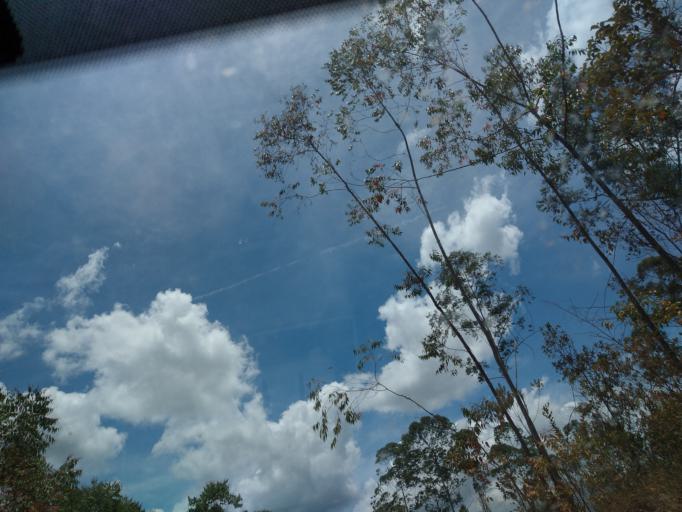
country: BR
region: Minas Gerais
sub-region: Sao Joao Del Rei
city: Sao Joao del Rei
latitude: -20.9043
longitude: -44.2920
